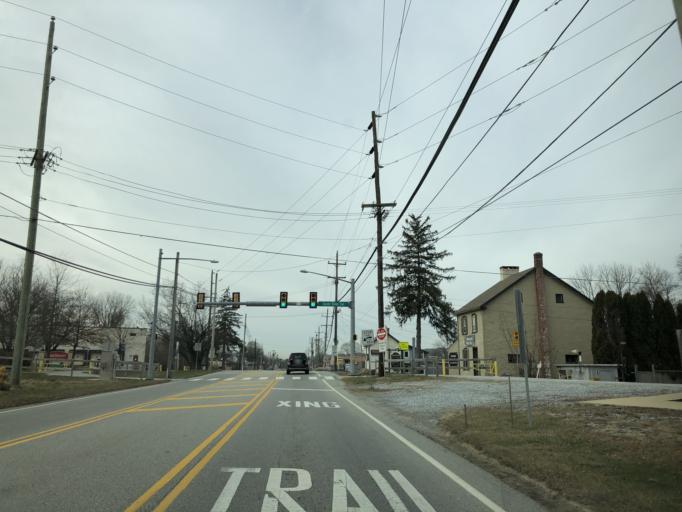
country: US
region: Pennsylvania
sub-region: Chester County
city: Exton
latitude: 40.0292
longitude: -75.6178
